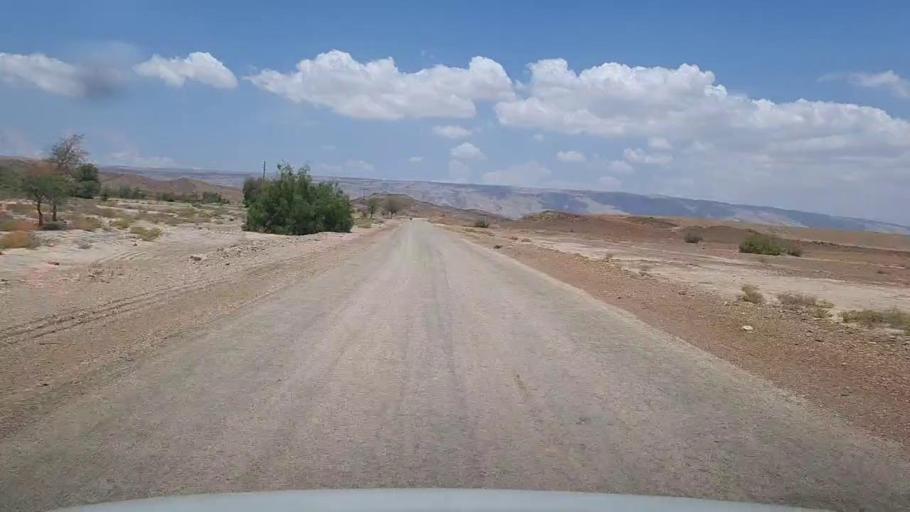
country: PK
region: Sindh
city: Bhan
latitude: 26.3172
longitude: 67.5719
